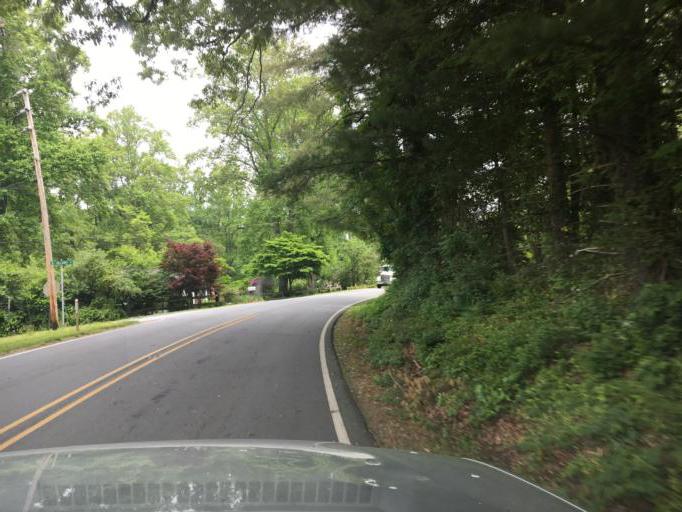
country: US
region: North Carolina
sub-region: Henderson County
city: Mountain Home
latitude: 35.3651
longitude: -82.4801
